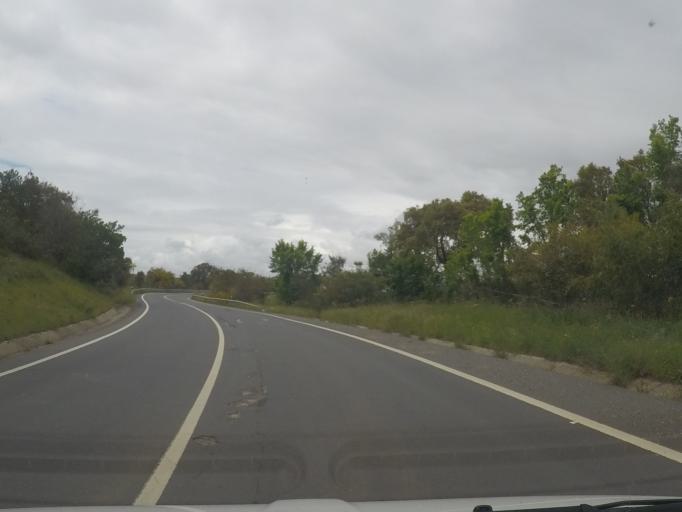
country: PT
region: Setubal
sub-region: Santiago do Cacem
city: Cercal
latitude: 37.8360
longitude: -8.7037
